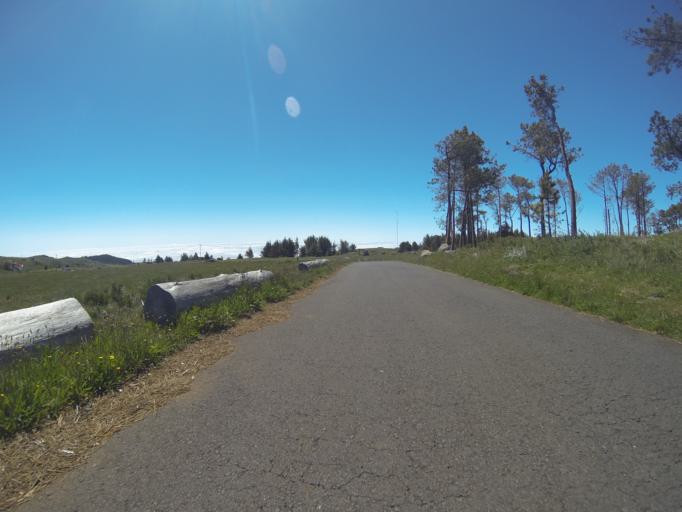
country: PT
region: Madeira
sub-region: Funchal
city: Nossa Senhora do Monte
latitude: 32.7140
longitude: -16.9102
